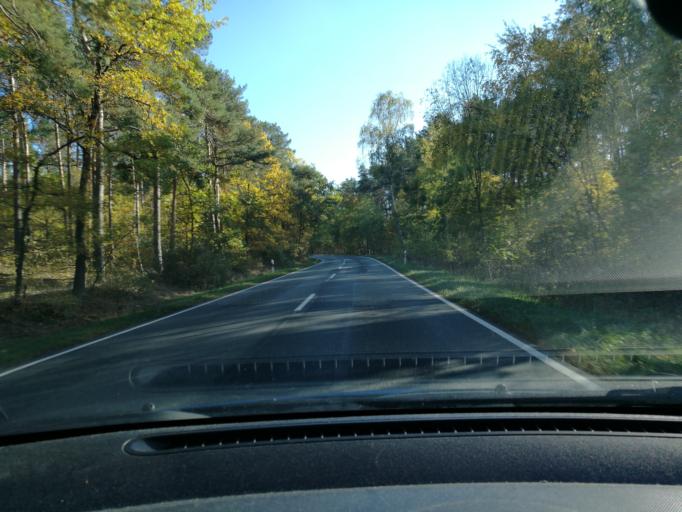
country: DE
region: Lower Saxony
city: Boitze
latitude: 53.1725
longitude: 10.7760
